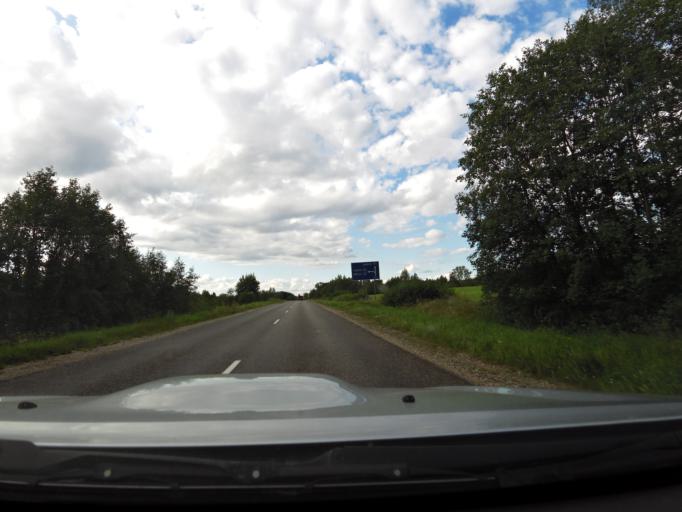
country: LV
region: Akniste
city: Akniste
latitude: 56.0199
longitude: 25.9225
